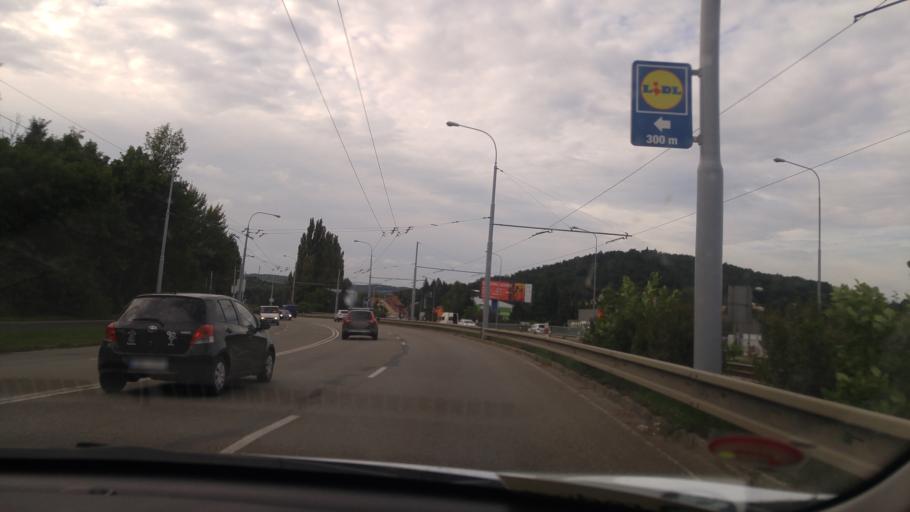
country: CZ
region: South Moravian
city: Troubsko
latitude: 49.2248
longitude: 16.5360
